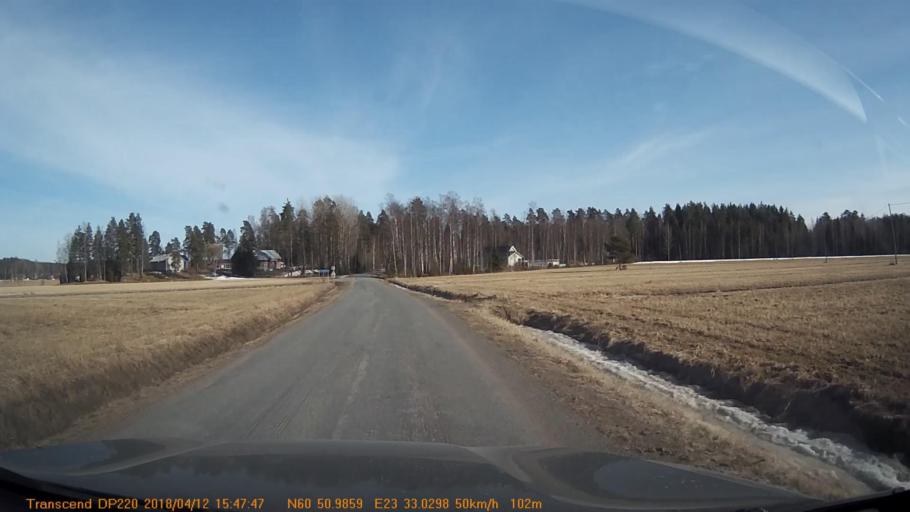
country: FI
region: Haeme
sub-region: Forssa
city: Forssa
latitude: 60.8496
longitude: 23.5510
